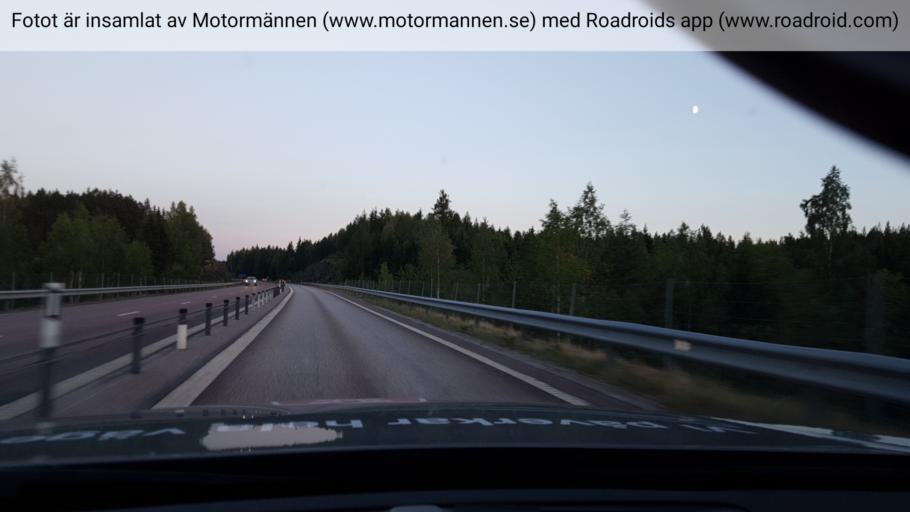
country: SE
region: Vaestmanland
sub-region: Surahammars Kommun
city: Ramnas
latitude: 59.7790
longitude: 16.1491
